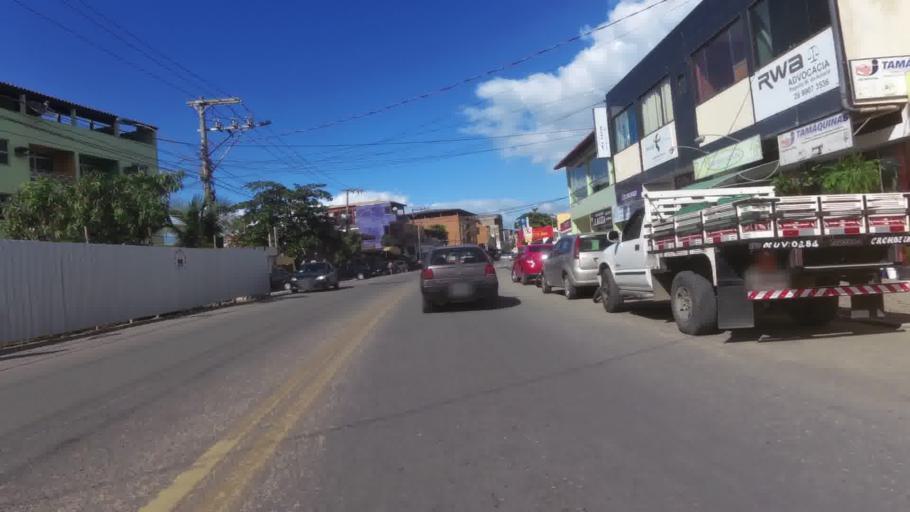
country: BR
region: Espirito Santo
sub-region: Marataizes
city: Marataizes
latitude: -21.0342
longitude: -40.8182
